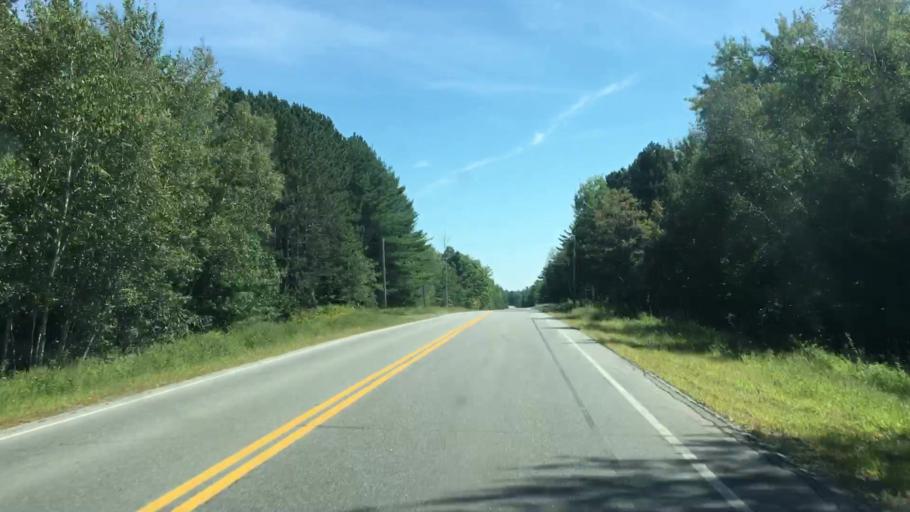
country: US
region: Maine
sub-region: Piscataquis County
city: Milo
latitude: 45.2277
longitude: -68.9321
